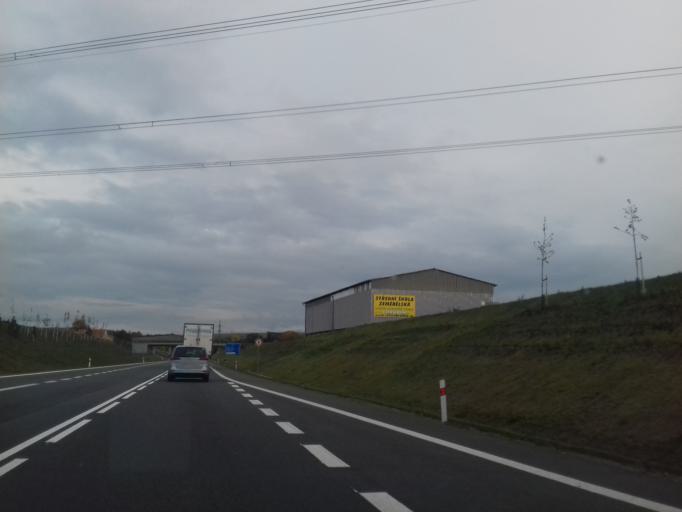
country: CZ
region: Pardubicky
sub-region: Okres Chrudim
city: Chrudim
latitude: 49.9686
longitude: 15.8013
